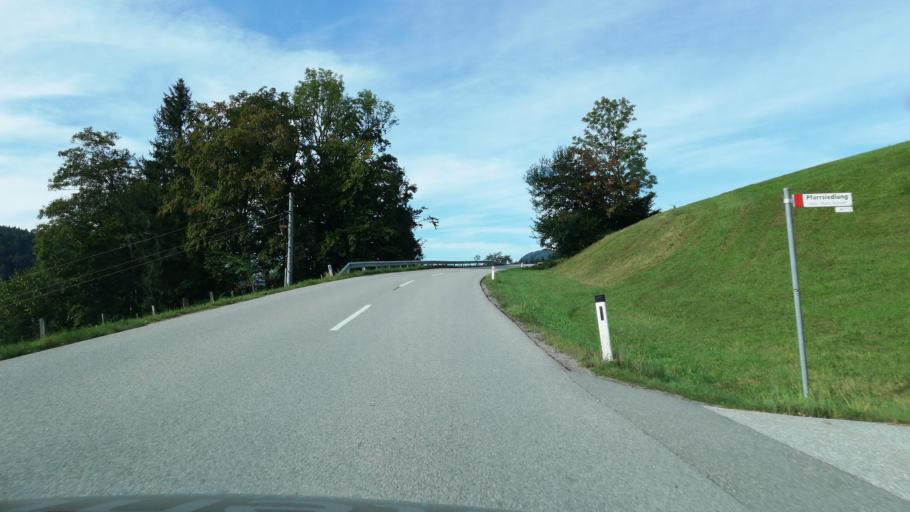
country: AT
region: Upper Austria
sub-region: Politischer Bezirk Steyr-Land
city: Maria Neustift
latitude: 47.9339
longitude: 14.6089
